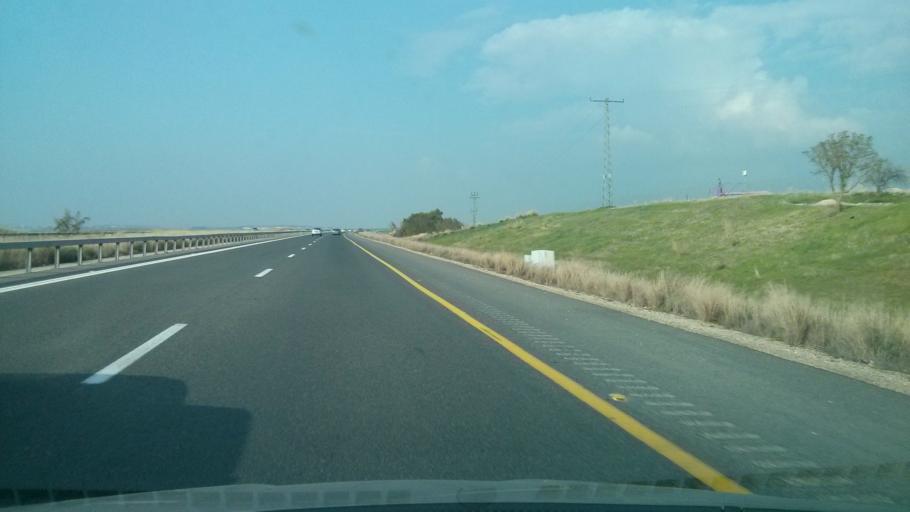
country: IL
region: Central District
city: Bene 'Ayish
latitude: 31.7166
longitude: 34.8207
